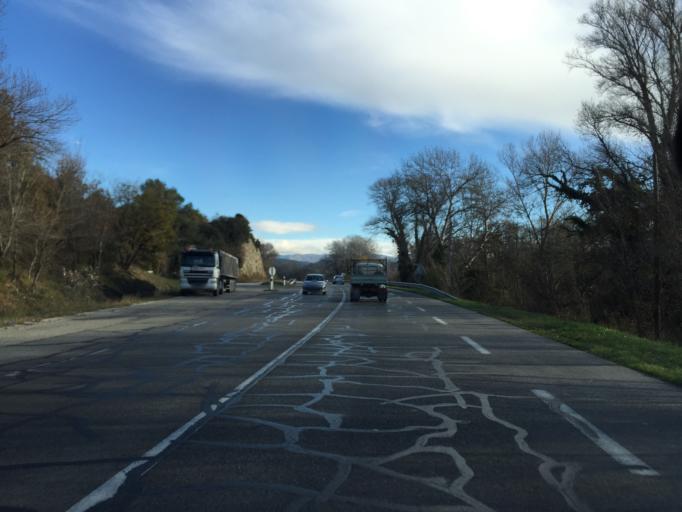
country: FR
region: Provence-Alpes-Cote d'Azur
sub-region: Departement du Vaucluse
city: Goult
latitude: 43.8556
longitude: 5.2458
